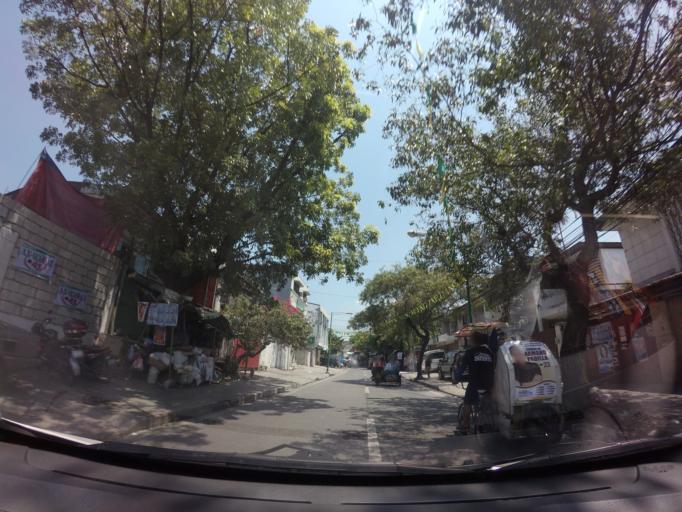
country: PH
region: Metro Manila
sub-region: Makati City
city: Makati City
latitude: 14.5605
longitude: 121.0028
